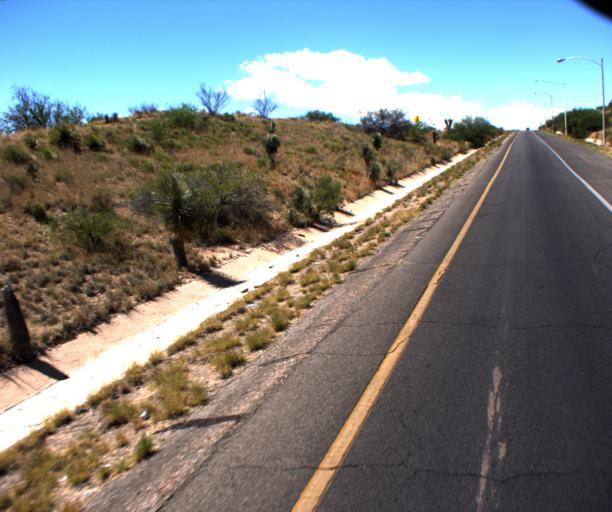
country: US
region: Arizona
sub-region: Cochise County
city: Whetstone
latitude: 31.9727
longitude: -110.3264
